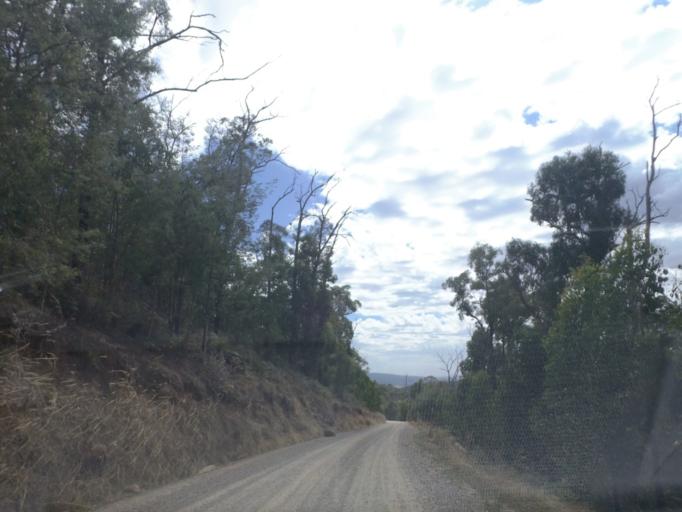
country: AU
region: Victoria
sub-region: Murrindindi
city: Alexandra
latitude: -37.4573
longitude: 145.7609
